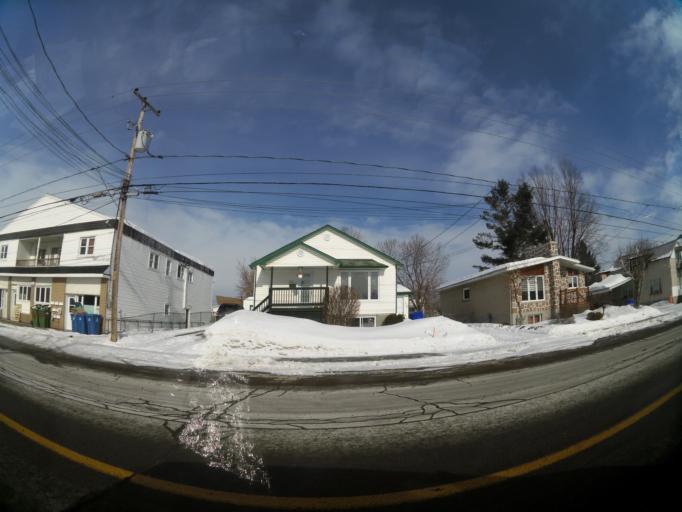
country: CA
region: Quebec
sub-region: Outaouais
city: Gatineau
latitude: 45.4809
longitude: -75.6257
